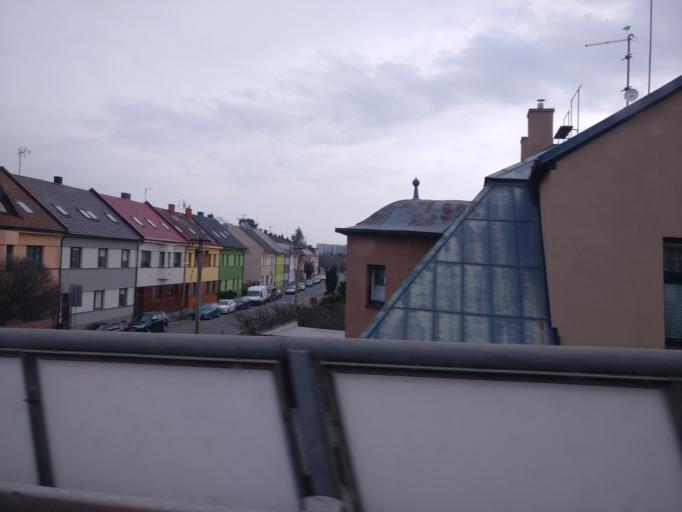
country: CZ
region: Pardubicky
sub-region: Okres Pardubice
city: Pardubice
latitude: 50.0325
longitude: 15.7893
